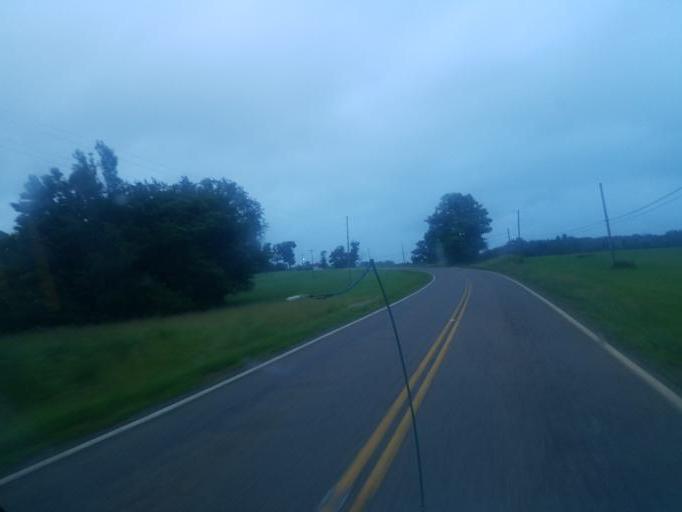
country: US
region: Ohio
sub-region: Columbiana County
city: Salineville
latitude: 40.6177
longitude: -80.9420
